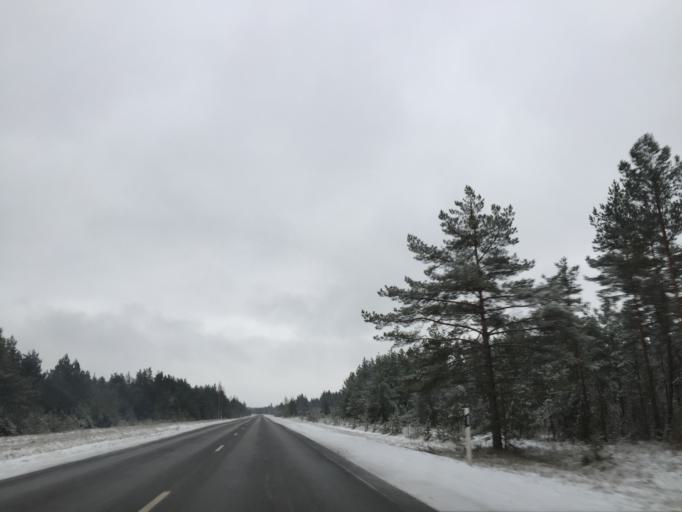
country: EE
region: Laeaene
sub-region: Lihula vald
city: Lihula
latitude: 58.6180
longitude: 23.9101
